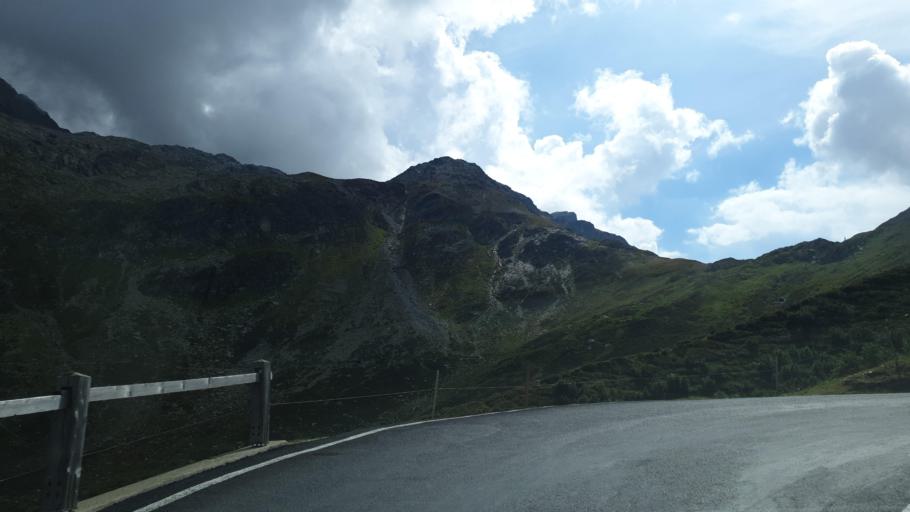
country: IT
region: Lombardy
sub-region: Provincia di Sondrio
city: Campodolcino
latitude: 46.5154
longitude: 9.3294
